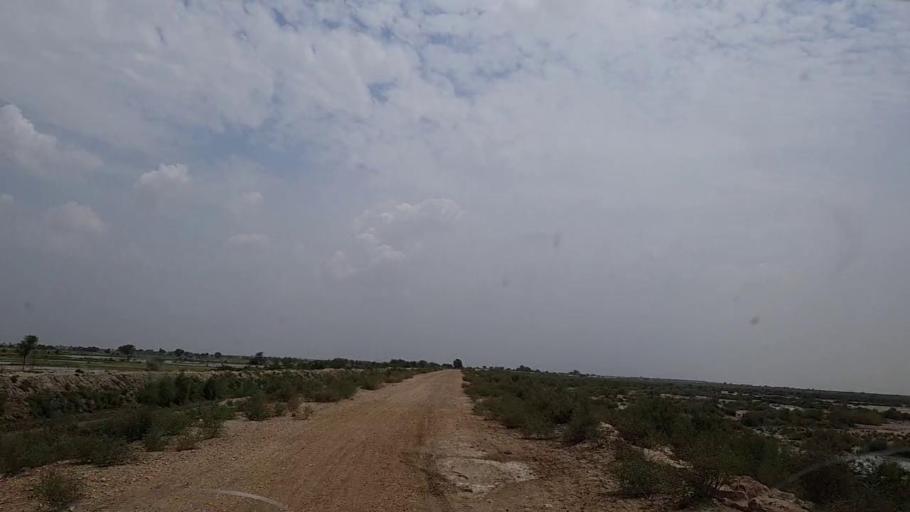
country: PK
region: Sindh
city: Phulji
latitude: 26.8357
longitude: 67.6177
